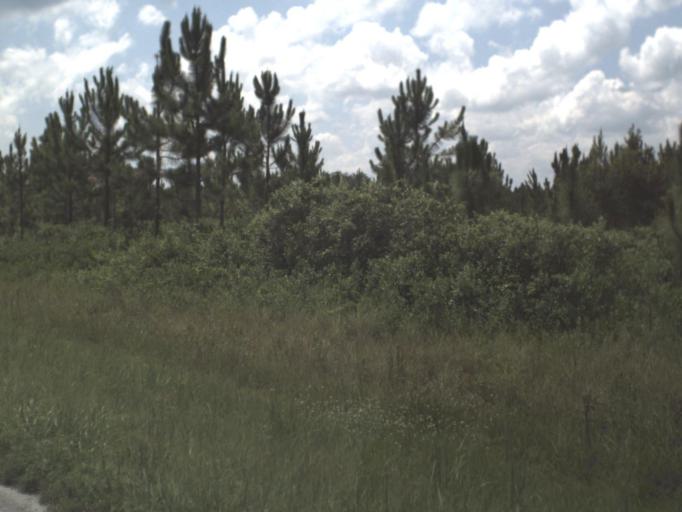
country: US
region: Florida
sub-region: Baker County
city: Macclenny
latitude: 30.5147
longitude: -82.2421
